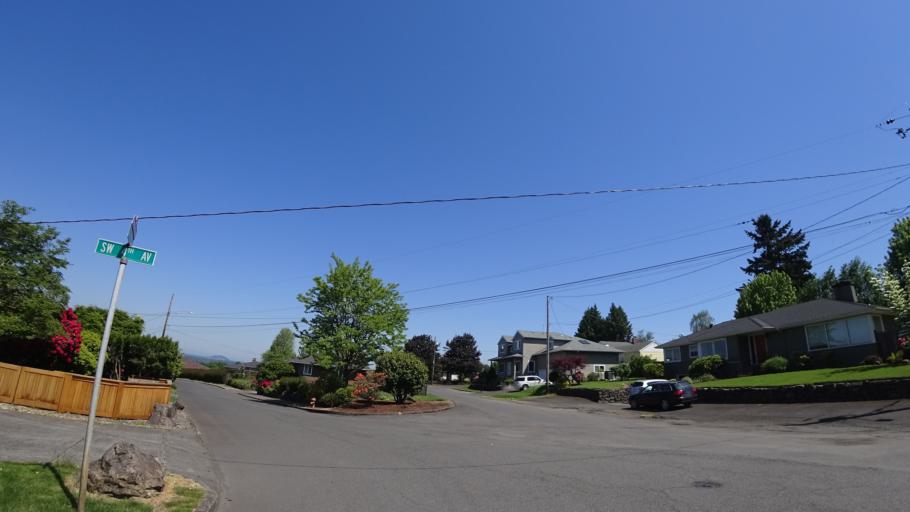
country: US
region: Oregon
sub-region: Clackamas County
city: Lake Oswego
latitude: 45.4655
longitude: -122.6824
